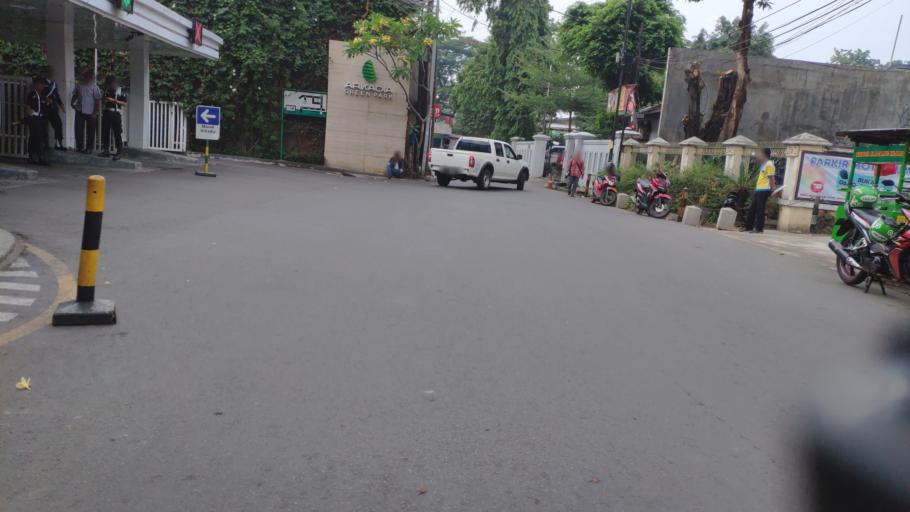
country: ID
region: Jakarta Raya
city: Jakarta
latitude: -6.3005
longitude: 106.8324
